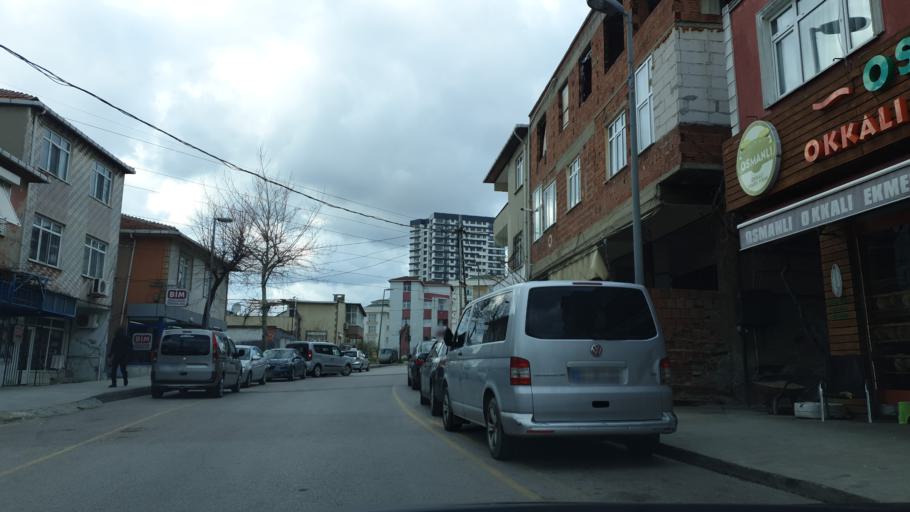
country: TR
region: Istanbul
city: Pendik
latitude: 40.8956
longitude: 29.2375
